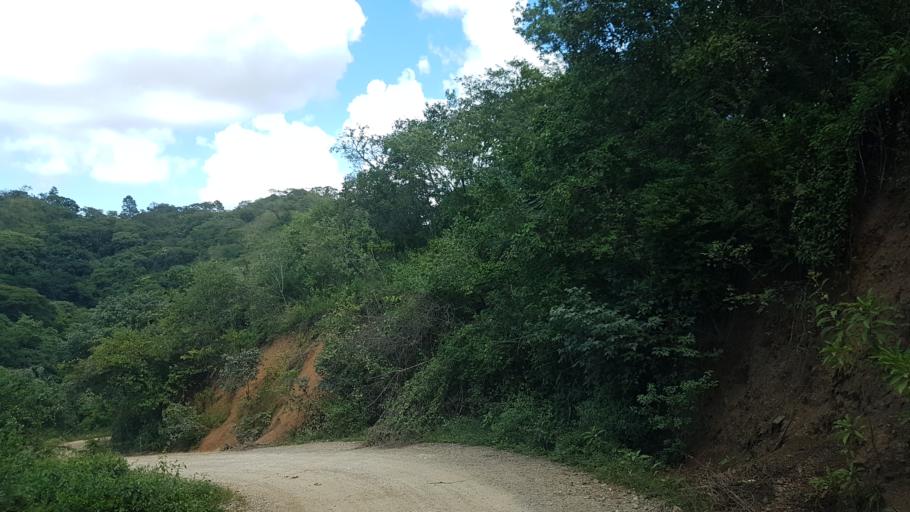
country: HN
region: El Paraiso
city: Oropoli
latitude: 13.7385
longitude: -86.7009
